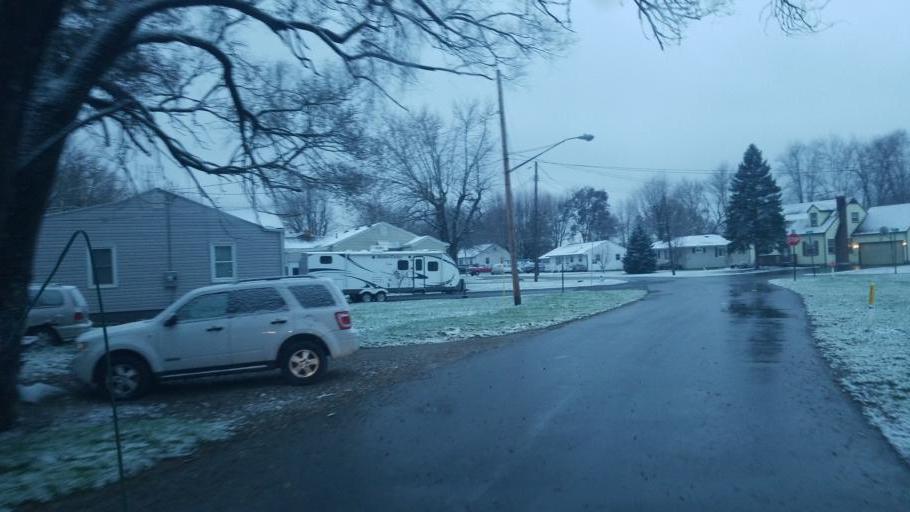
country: US
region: Ohio
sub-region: Marion County
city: Marion
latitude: 40.5838
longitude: -83.0991
